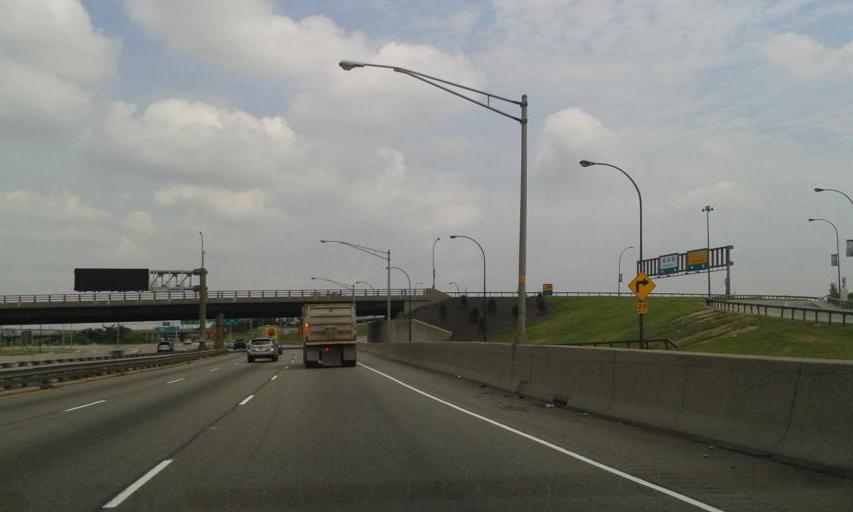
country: US
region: New Jersey
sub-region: Union County
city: Elizabeth
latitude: 40.6928
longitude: -74.1887
